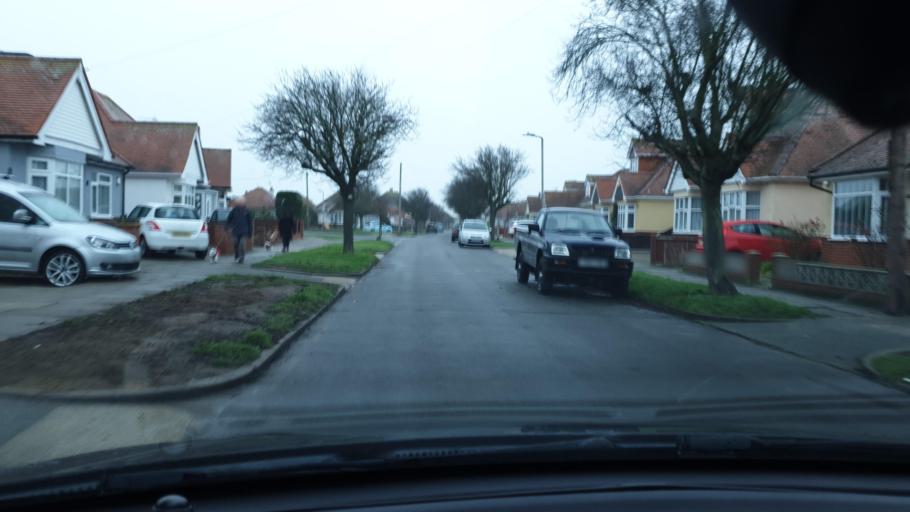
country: GB
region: England
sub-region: Essex
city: Clacton-on-Sea
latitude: 51.8025
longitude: 1.1916
